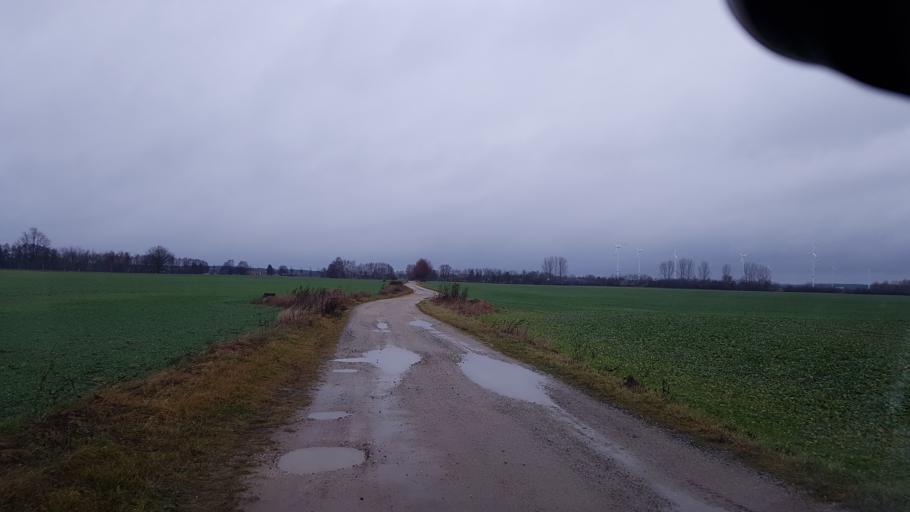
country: DE
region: Brandenburg
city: Sallgast
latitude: 51.6296
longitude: 13.8481
